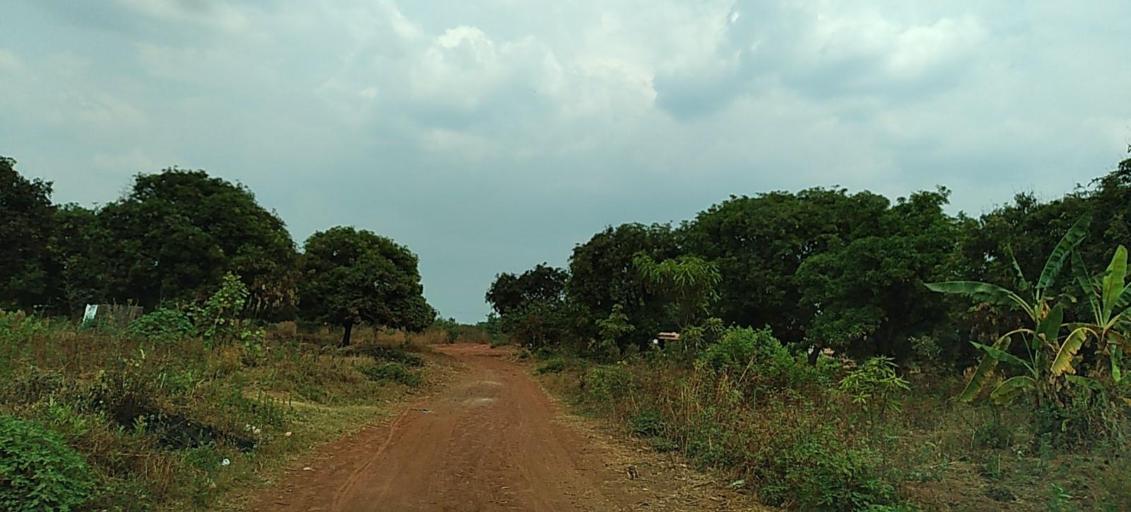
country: ZM
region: Copperbelt
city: Kalulushi
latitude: -12.8927
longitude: 28.0786
